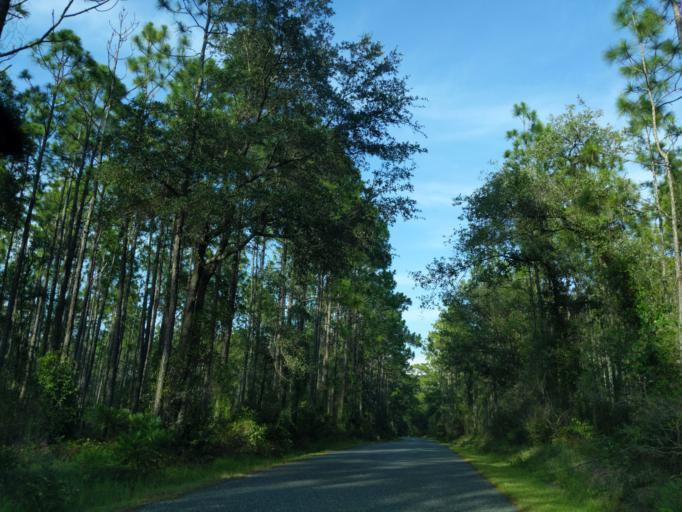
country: US
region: Florida
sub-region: Leon County
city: Woodville
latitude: 30.3472
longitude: -84.3706
